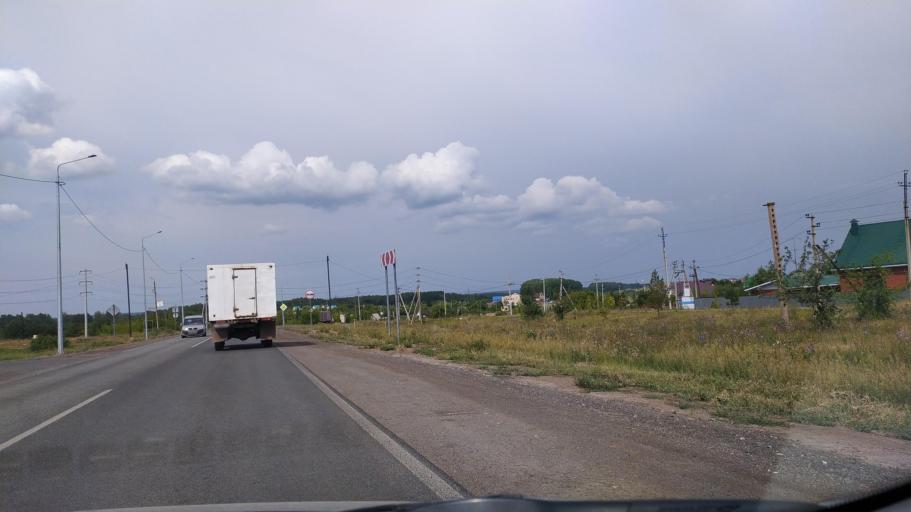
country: RU
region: Tatarstan
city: Al'met'yevsk
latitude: 54.8847
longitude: 52.2555
